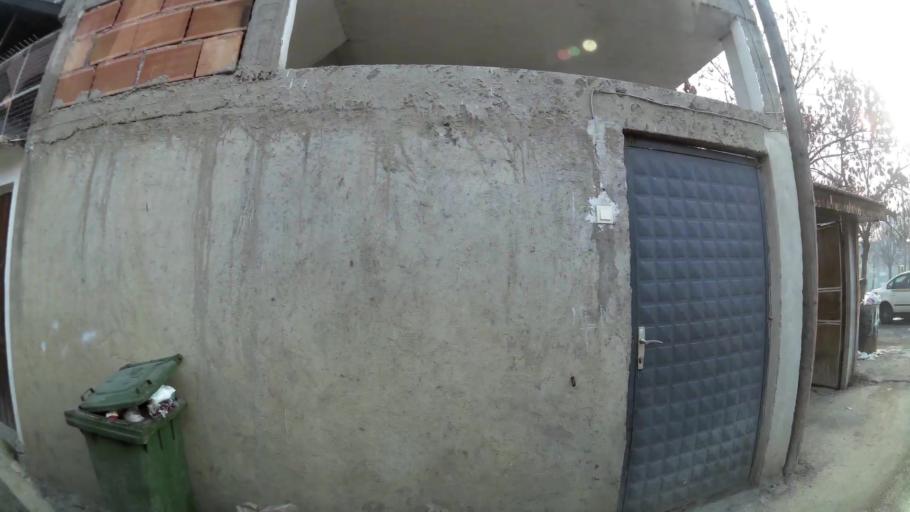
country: MK
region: Cair
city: Cair
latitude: 42.0210
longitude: 21.4383
